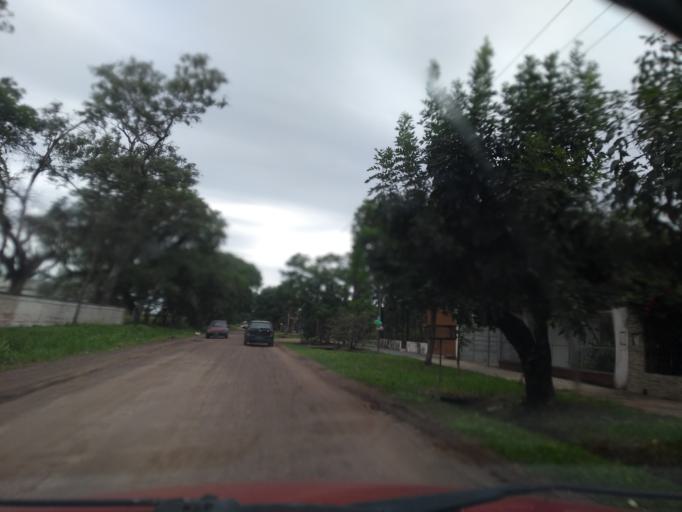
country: AR
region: Chaco
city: Barranqueras
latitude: -27.4779
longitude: -58.9592
